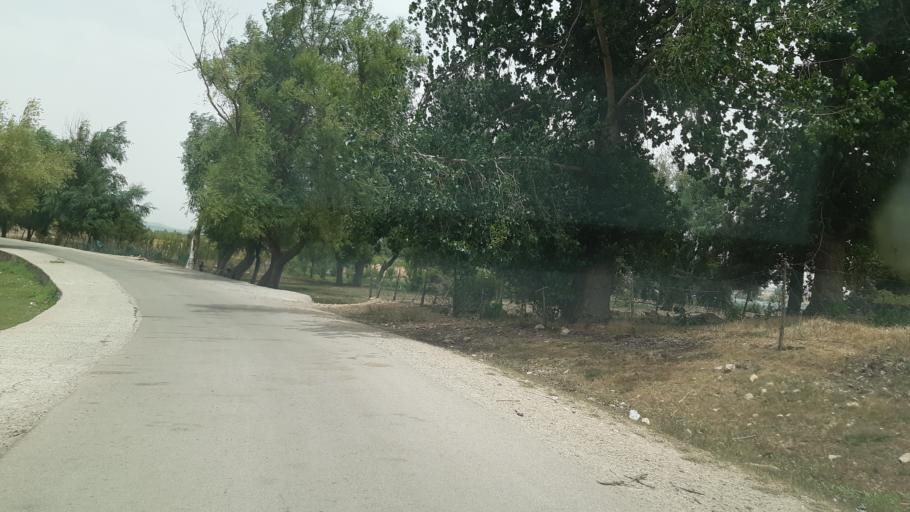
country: MA
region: Meknes-Tafilalet
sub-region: Ifrane
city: Ifrane
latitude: 33.6488
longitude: -5.0129
